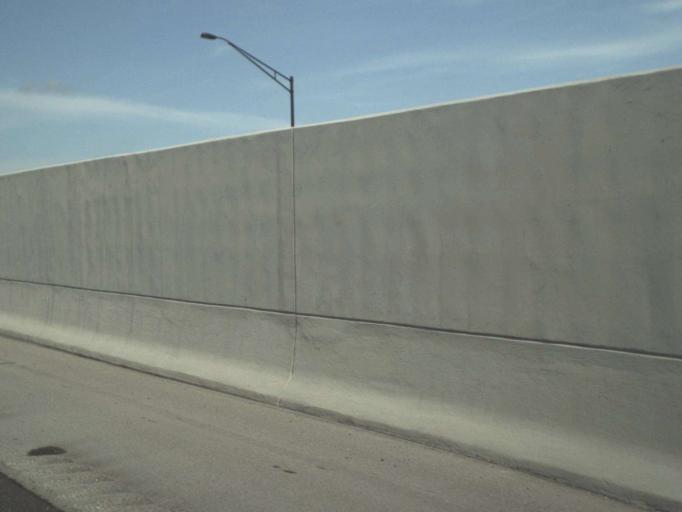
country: US
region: Florida
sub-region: Broward County
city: Broadview Park
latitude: 26.0938
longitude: -80.2275
